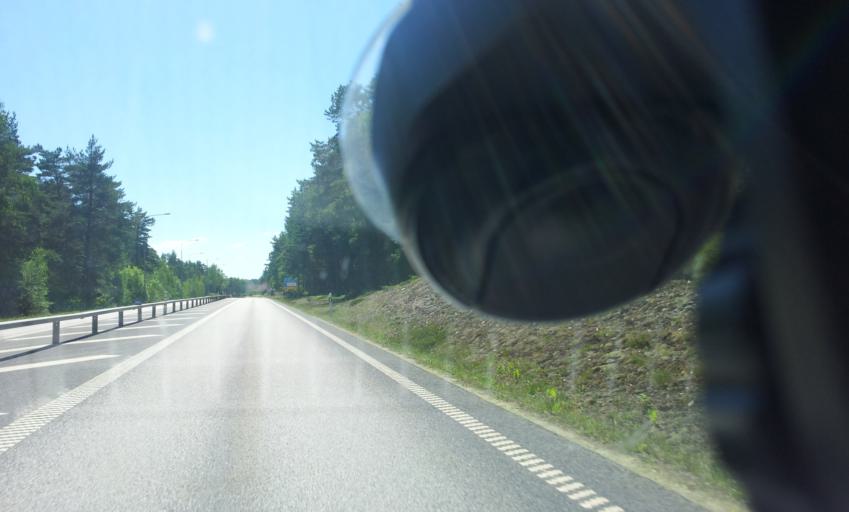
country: SE
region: Kalmar
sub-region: Vasterviks Kommun
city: Forserum
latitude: 57.9971
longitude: 16.4865
